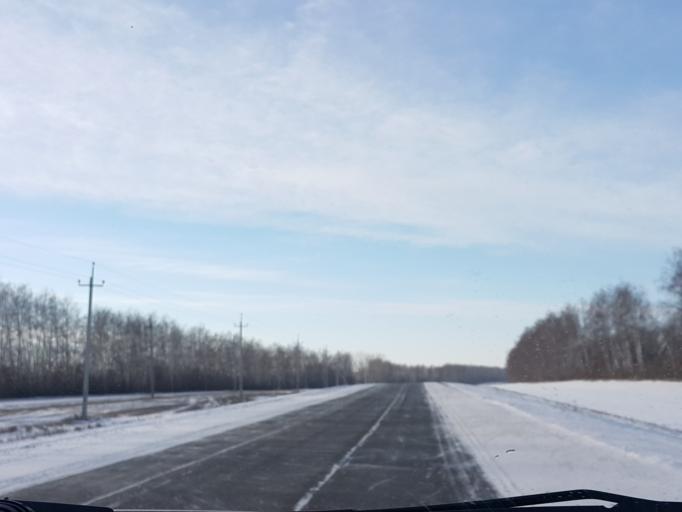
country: RU
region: Tambov
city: Znamenka
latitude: 52.3845
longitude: 41.3354
